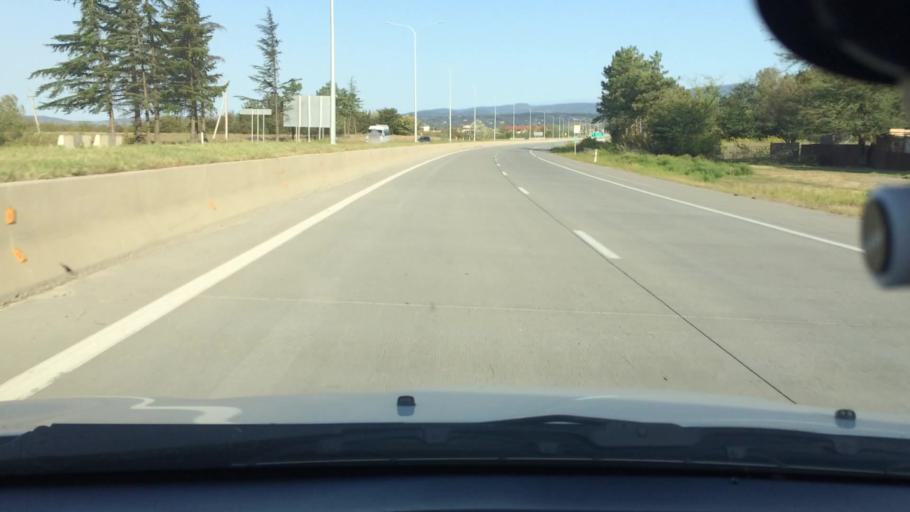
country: GE
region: Imereti
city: Zestap'oni
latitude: 42.1658
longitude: 42.9402
